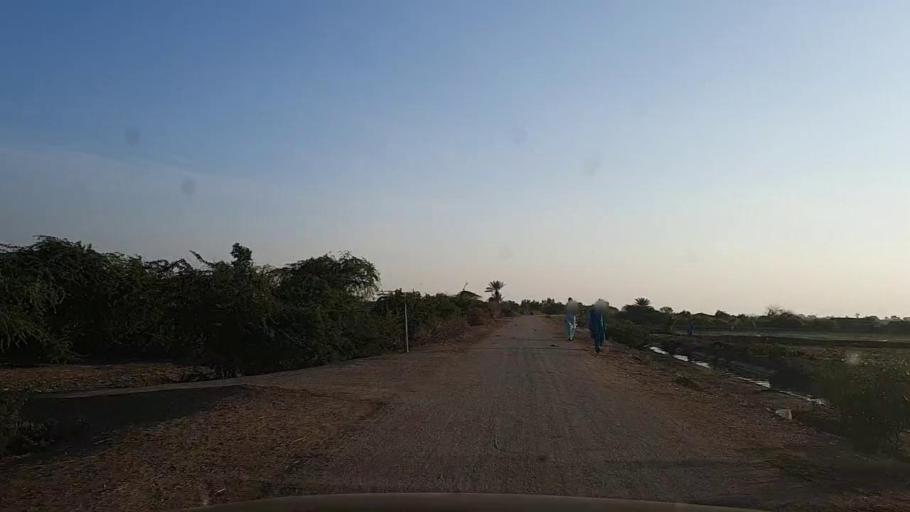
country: PK
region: Sindh
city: Thatta
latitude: 24.6229
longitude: 67.9140
